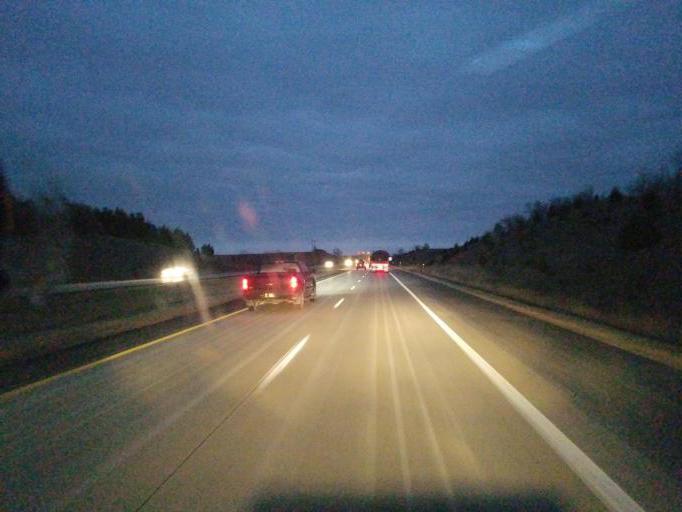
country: US
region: Iowa
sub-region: Cass County
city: Atlantic
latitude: 41.4966
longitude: -94.7738
